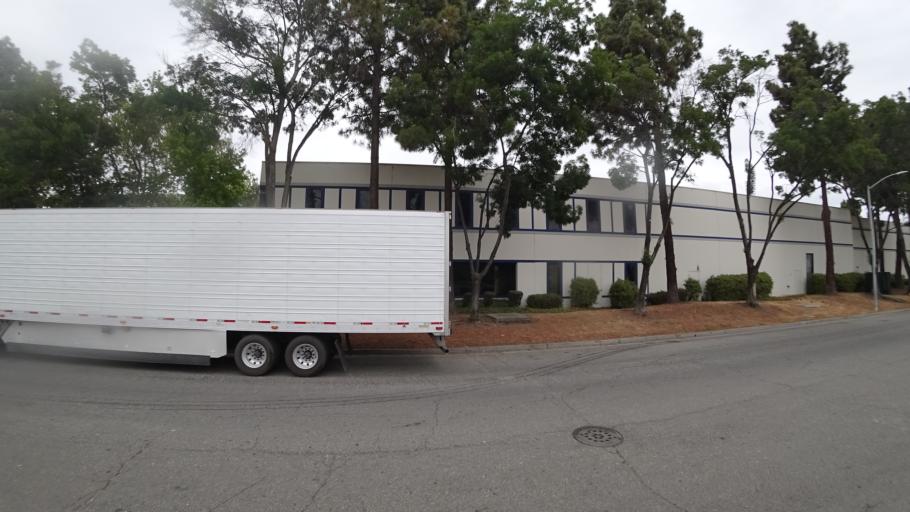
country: US
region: California
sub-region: Alameda County
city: Union City
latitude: 37.6105
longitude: -122.0613
